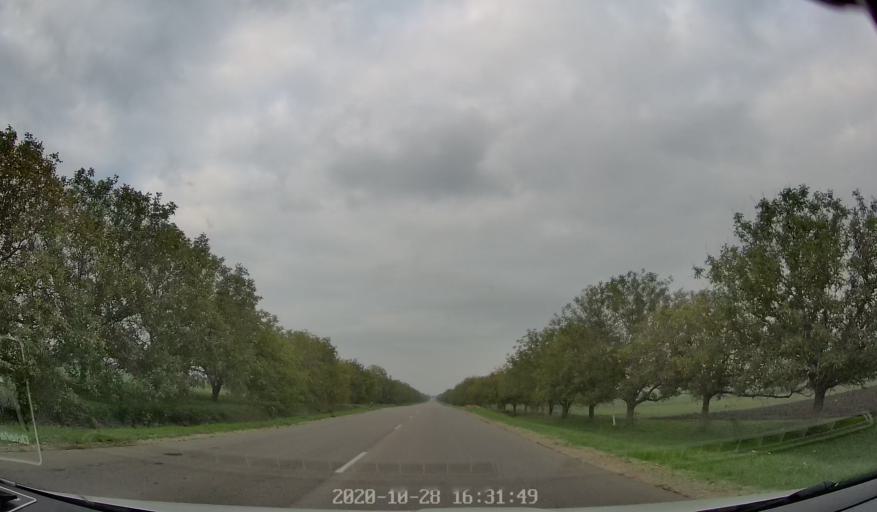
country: MD
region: Gagauzia
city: Comrat
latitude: 46.1520
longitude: 28.6212
